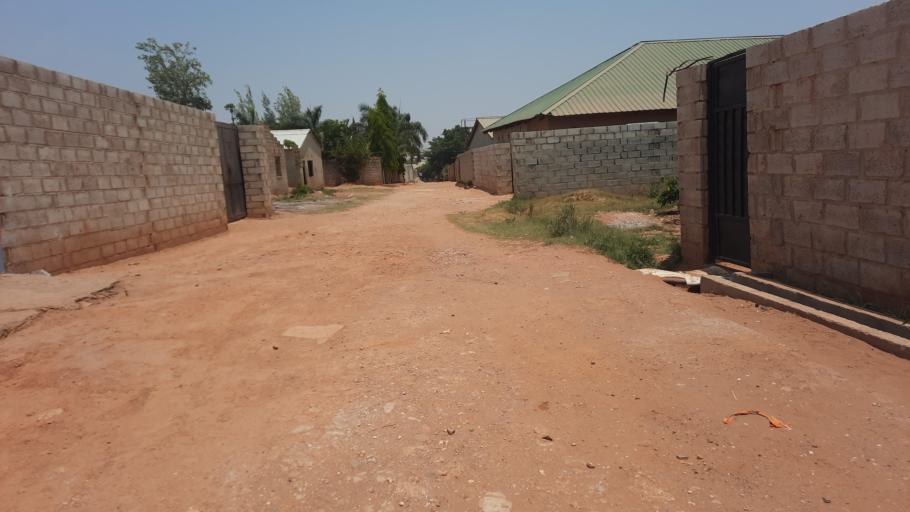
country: ZM
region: Lusaka
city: Lusaka
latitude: -15.4069
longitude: 28.3822
